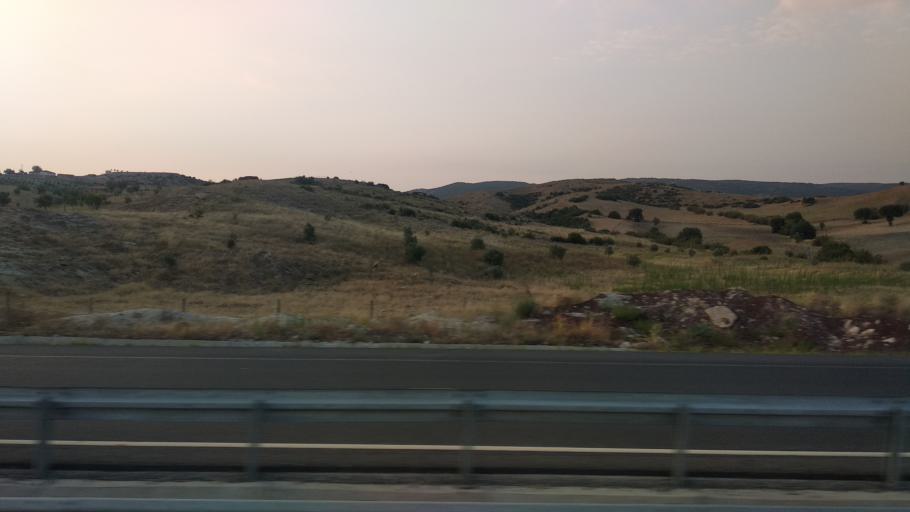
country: TR
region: Manisa
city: Selendi
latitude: 38.6272
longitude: 28.9330
